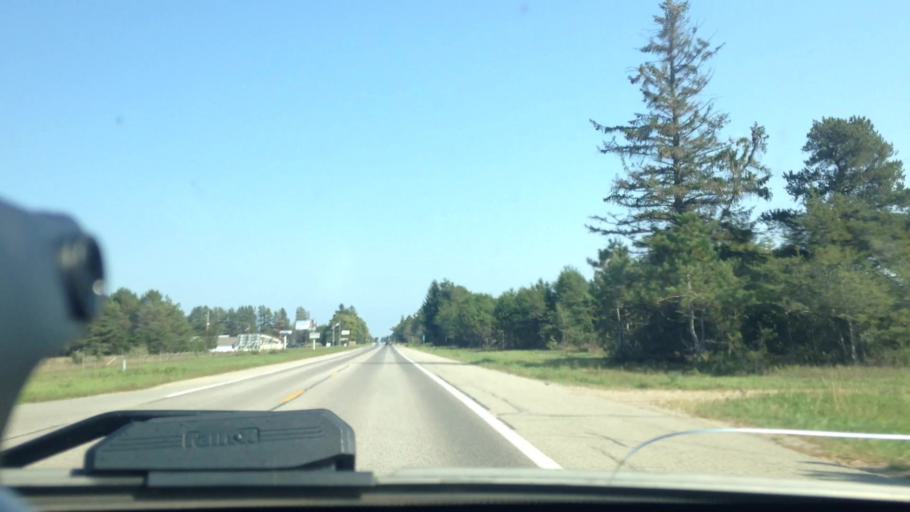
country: US
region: Michigan
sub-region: Luce County
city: Newberry
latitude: 46.3034
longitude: -85.4733
